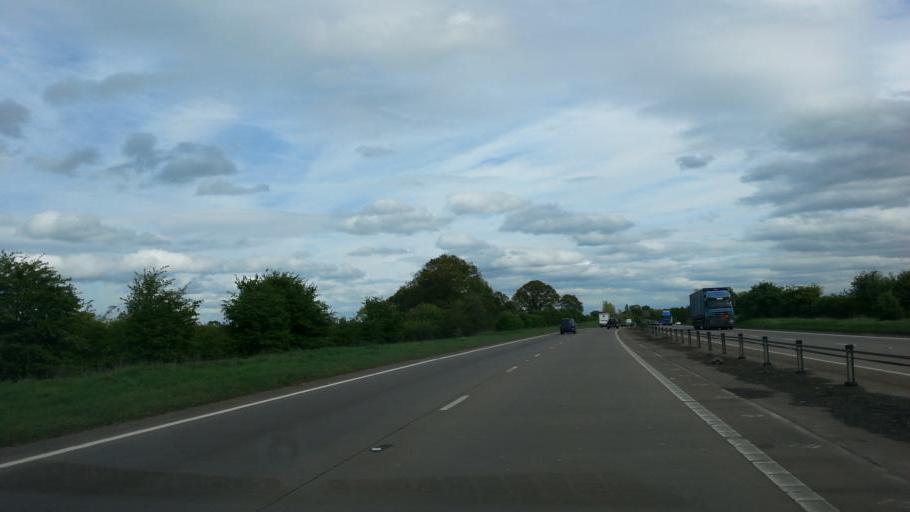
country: GB
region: England
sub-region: Staffordshire
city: Uttoxeter
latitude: 52.9013
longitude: -1.7995
